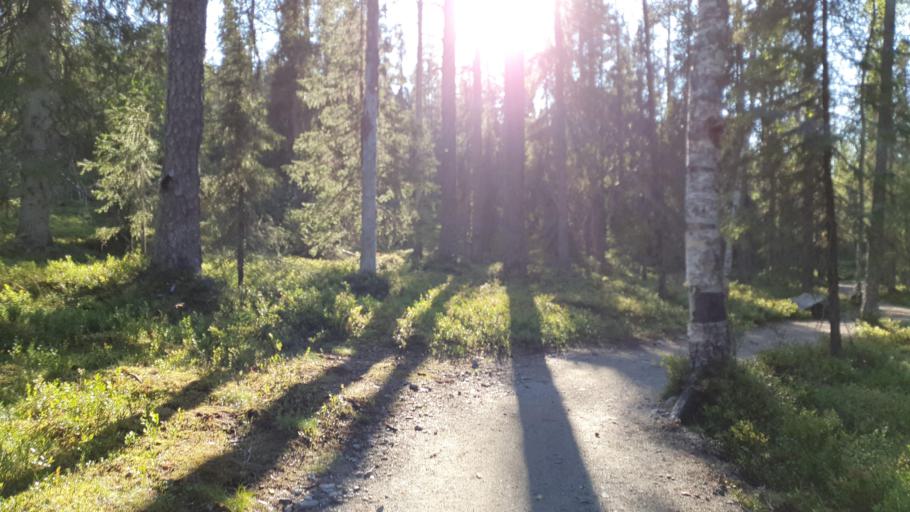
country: FI
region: Lapland
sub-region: Tunturi-Lappi
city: Kolari
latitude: 67.5961
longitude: 24.2349
